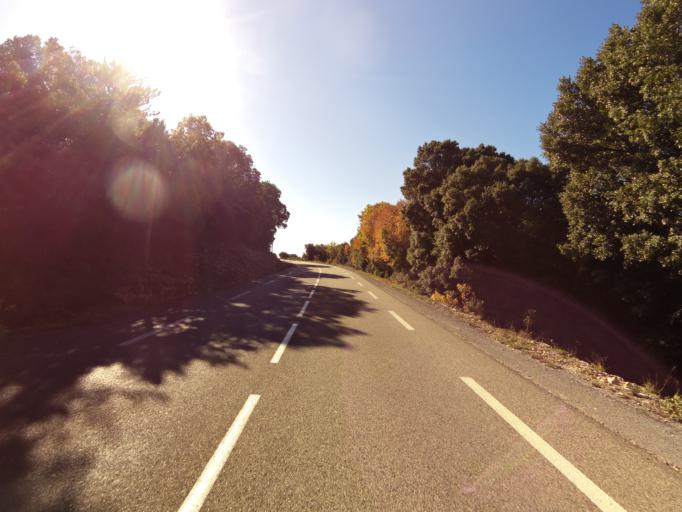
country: FR
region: Languedoc-Roussillon
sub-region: Departement du Gard
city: Saint-Julien-de-Peyrolas
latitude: 44.4011
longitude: 4.4810
